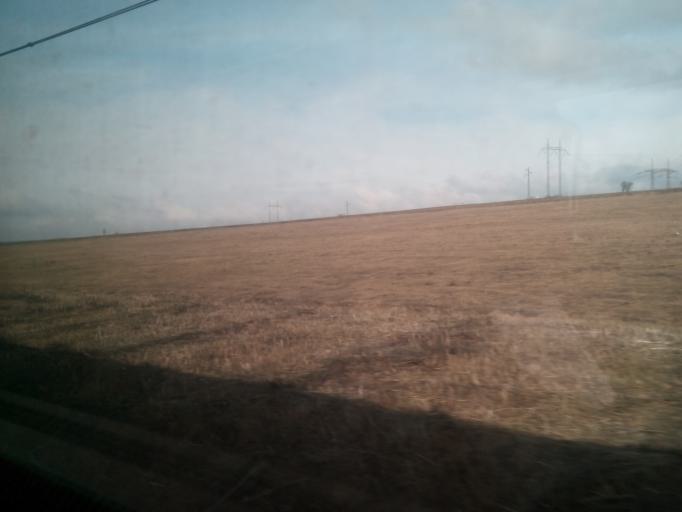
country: SK
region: Presovsky
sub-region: Okres Poprad
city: Strba
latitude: 49.0716
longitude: 20.0080
